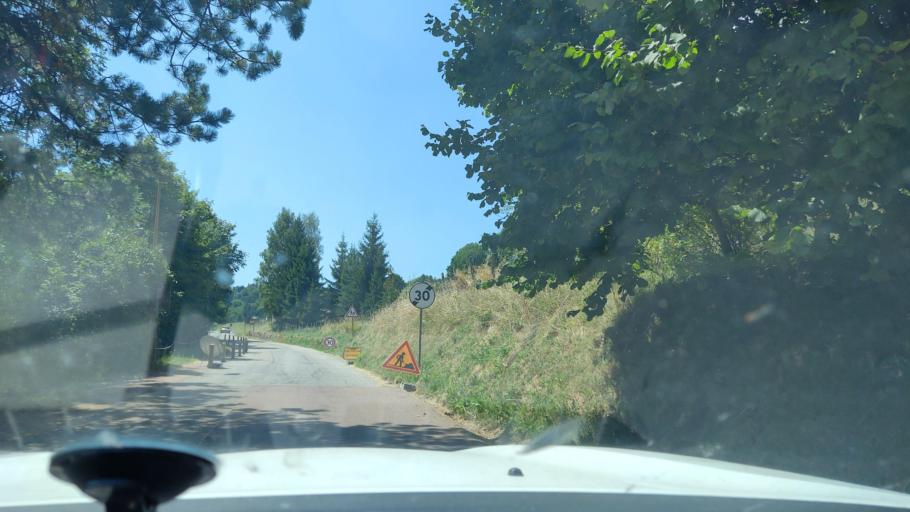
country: FR
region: Rhone-Alpes
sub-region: Departement de la Haute-Savoie
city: Cusy
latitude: 45.6671
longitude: 6.0355
